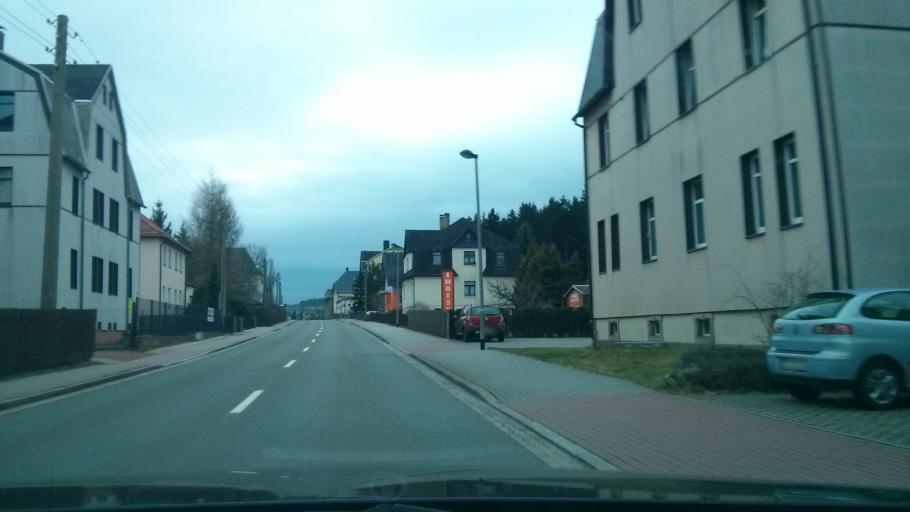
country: DE
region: Saxony
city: Oelsnitz
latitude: 50.7146
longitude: 12.7250
